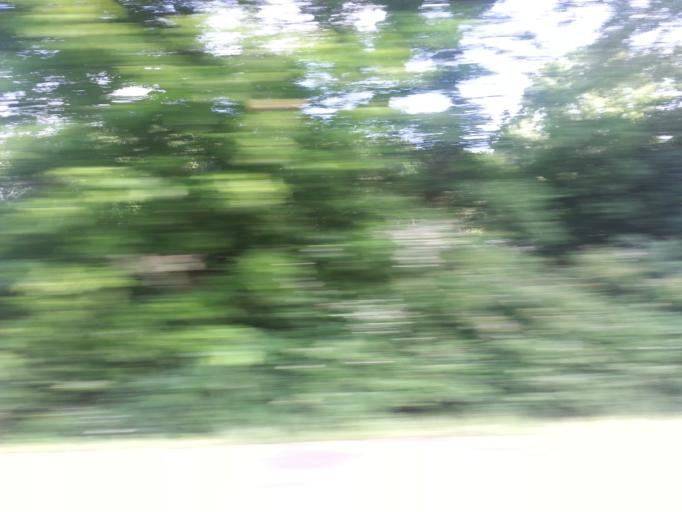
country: US
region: Tennessee
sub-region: Knox County
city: Knoxville
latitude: 36.0410
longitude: -83.8747
